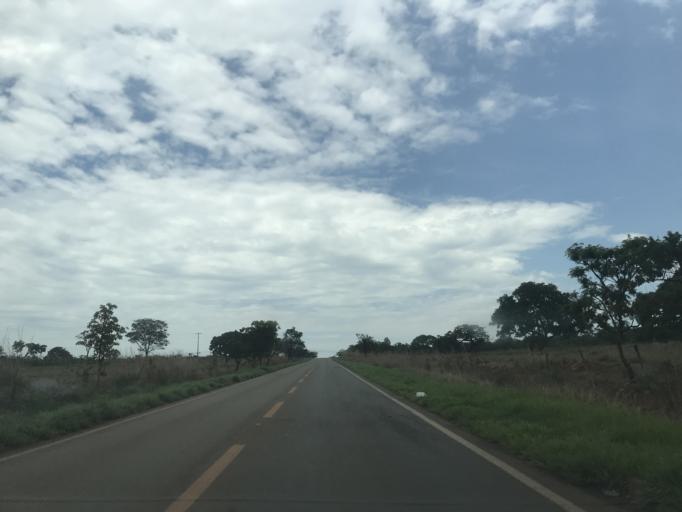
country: BR
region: Goias
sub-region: Luziania
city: Luziania
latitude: -16.2810
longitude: -47.9974
